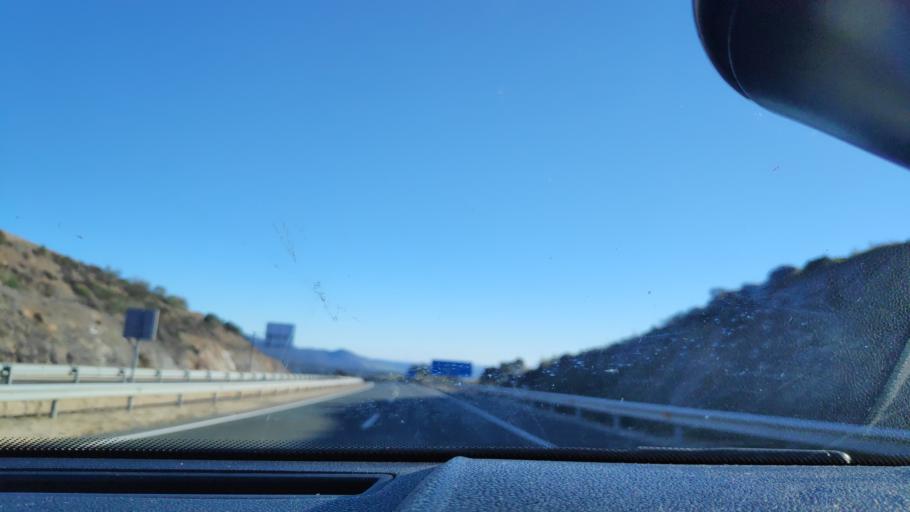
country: ES
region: Extremadura
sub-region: Provincia de Badajoz
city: Monesterio
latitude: 38.0767
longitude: -6.2569
